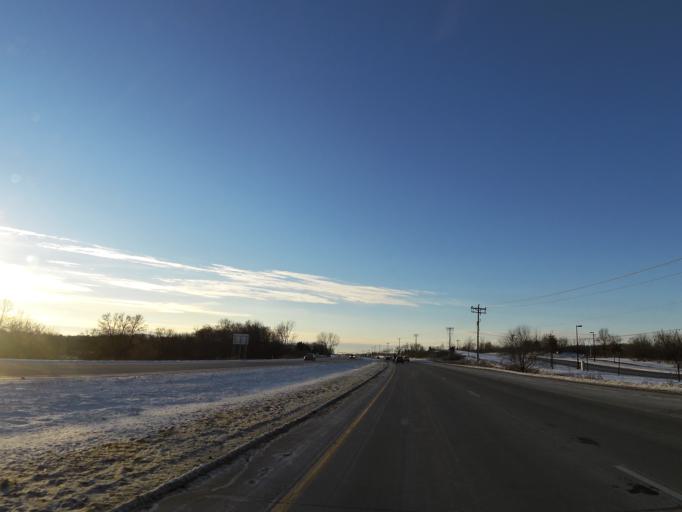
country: US
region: Minnesota
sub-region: Carver County
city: Chanhassen
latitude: 44.8622
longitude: -93.5505
